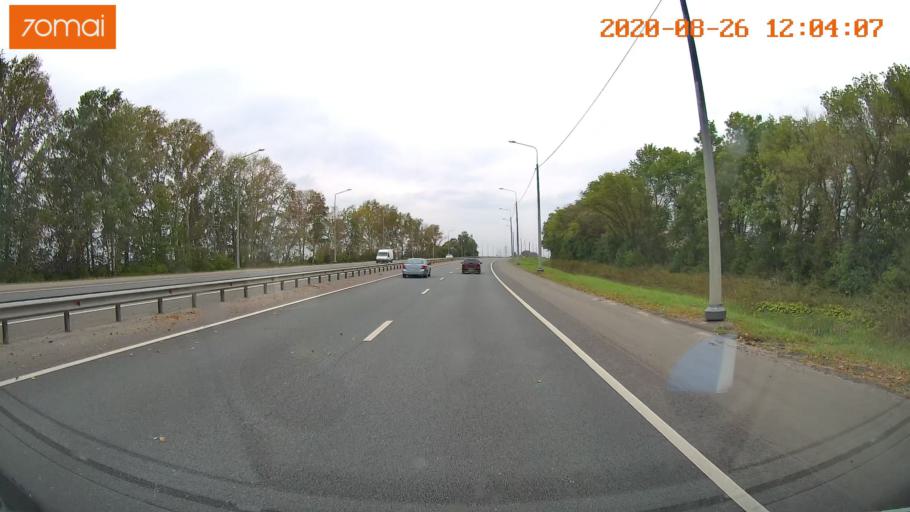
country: RU
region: Rjazan
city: Kiritsy
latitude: 54.3065
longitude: 40.1944
